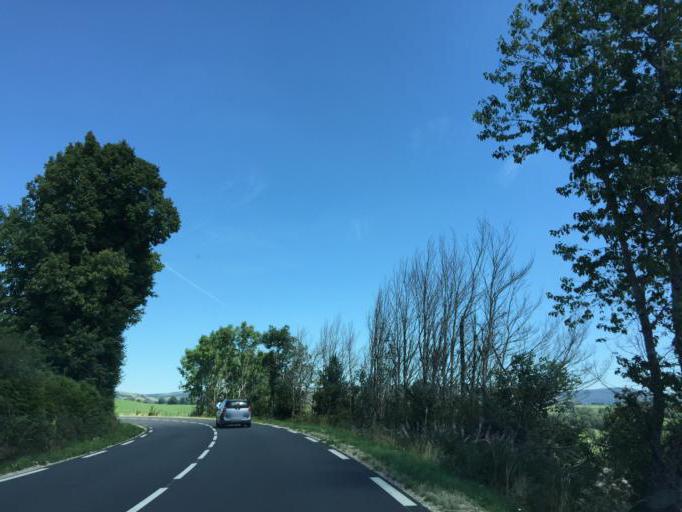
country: FR
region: Midi-Pyrenees
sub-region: Departement de l'Aveyron
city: Laguiole
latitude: 44.6251
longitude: 2.8248
